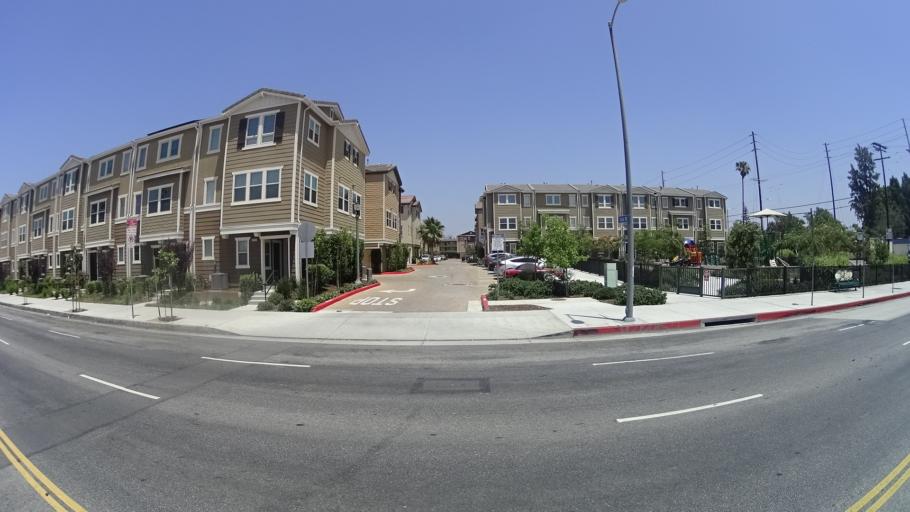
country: US
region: California
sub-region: Los Angeles County
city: Van Nuys
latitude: 34.2012
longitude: -118.4406
